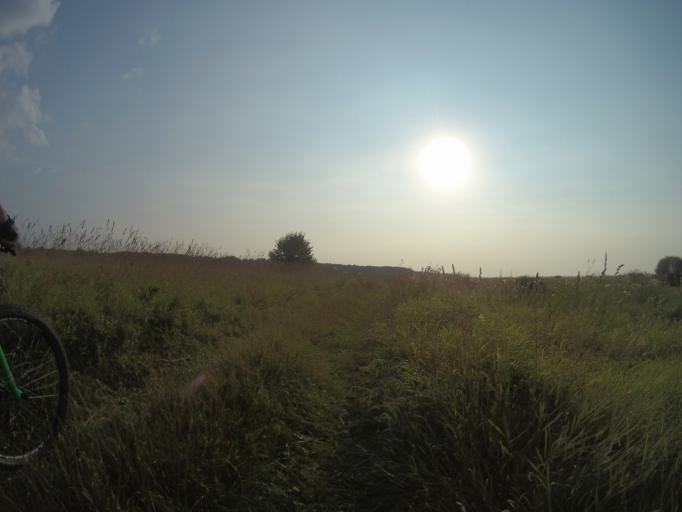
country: RU
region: Vladimir
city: Orgtrud
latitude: 56.3007
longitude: 40.6718
